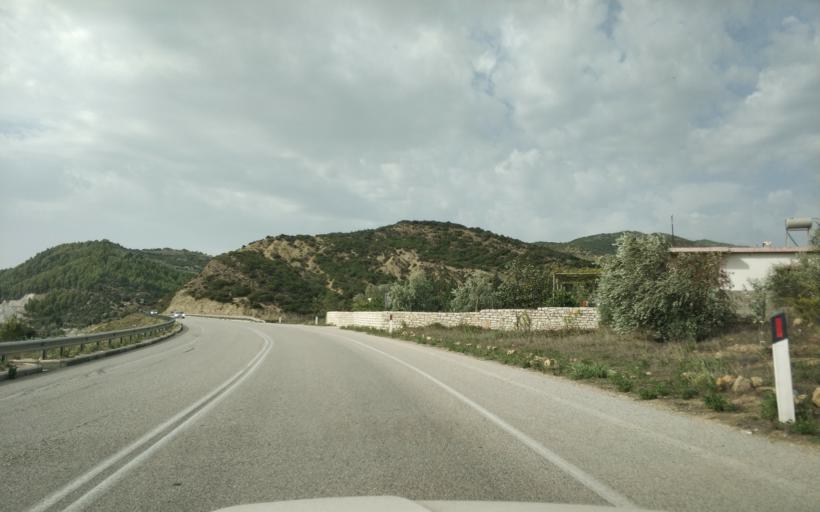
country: AL
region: Gjirokaster
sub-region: Rrethi i Tepelenes
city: Memaliaj
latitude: 40.3783
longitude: 19.9055
